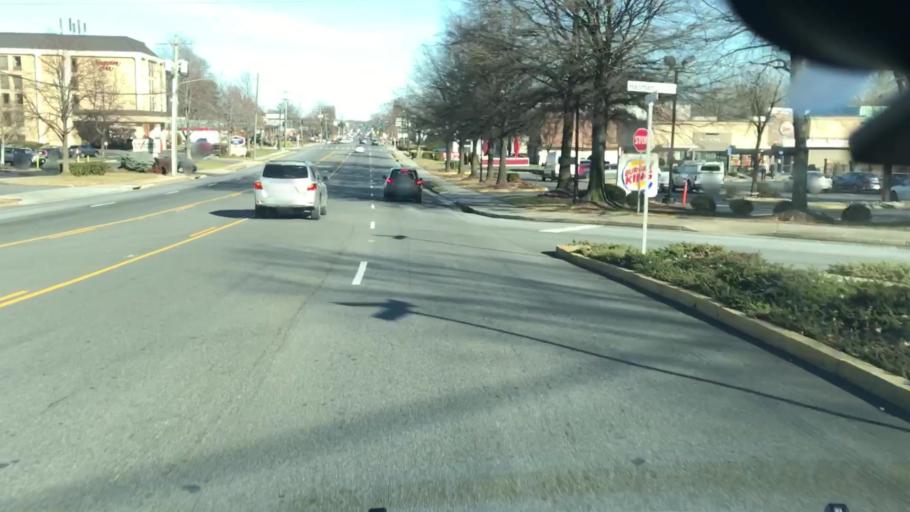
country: US
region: Virginia
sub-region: City of Fairfax
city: Fairfax
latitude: 38.8534
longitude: -77.3201
